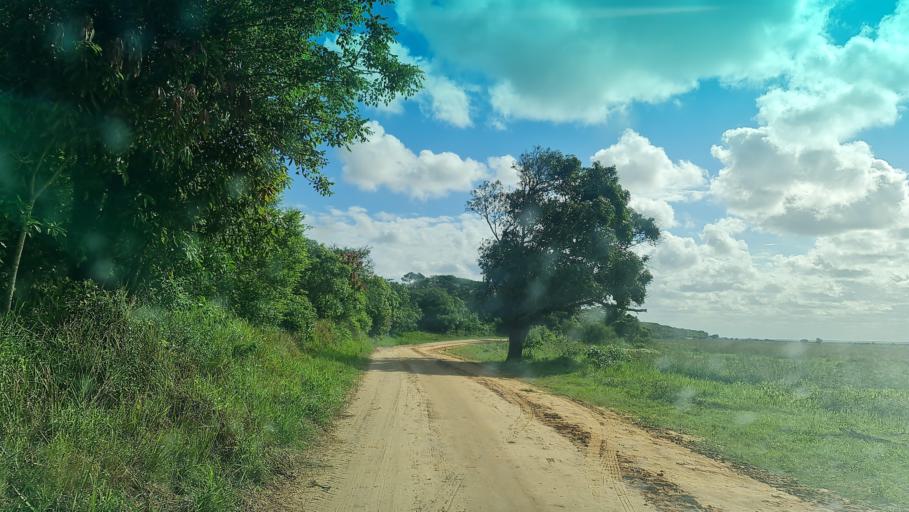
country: MZ
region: Maputo
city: Manhica
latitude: -25.4295
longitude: 32.8938
